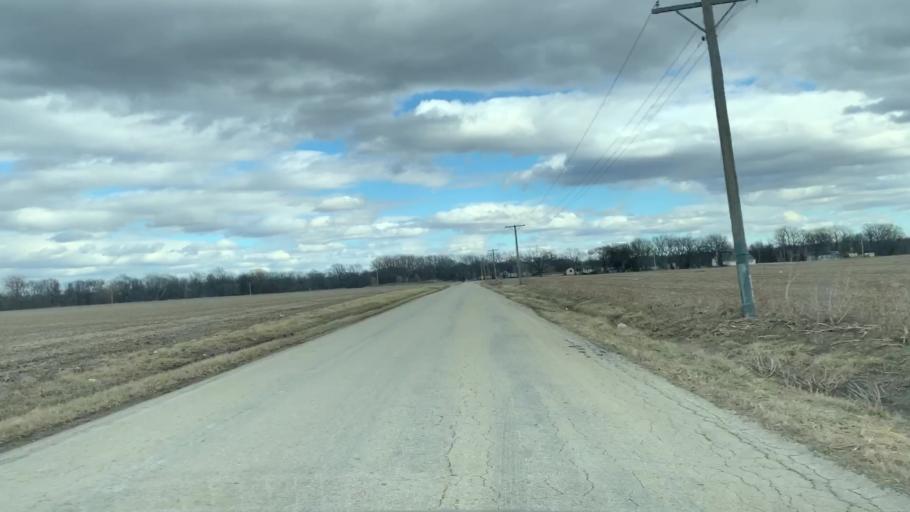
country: US
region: Kansas
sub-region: Allen County
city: Humboldt
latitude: 37.8129
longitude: -95.4576
